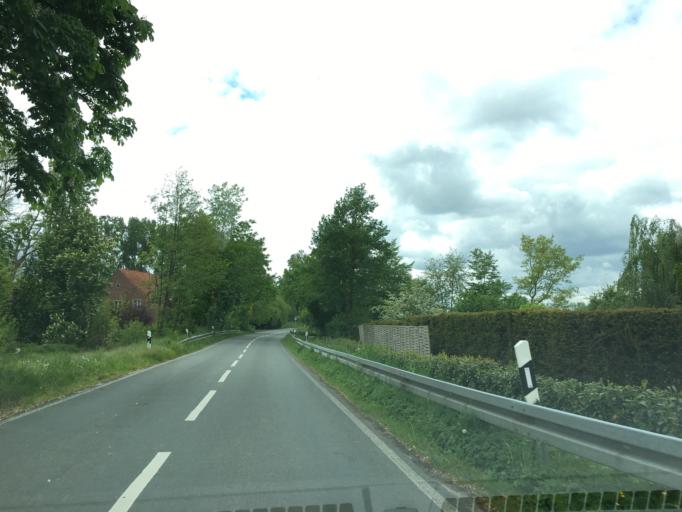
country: DE
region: North Rhine-Westphalia
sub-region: Regierungsbezirk Munster
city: Altenberge
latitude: 51.9799
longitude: 7.5137
